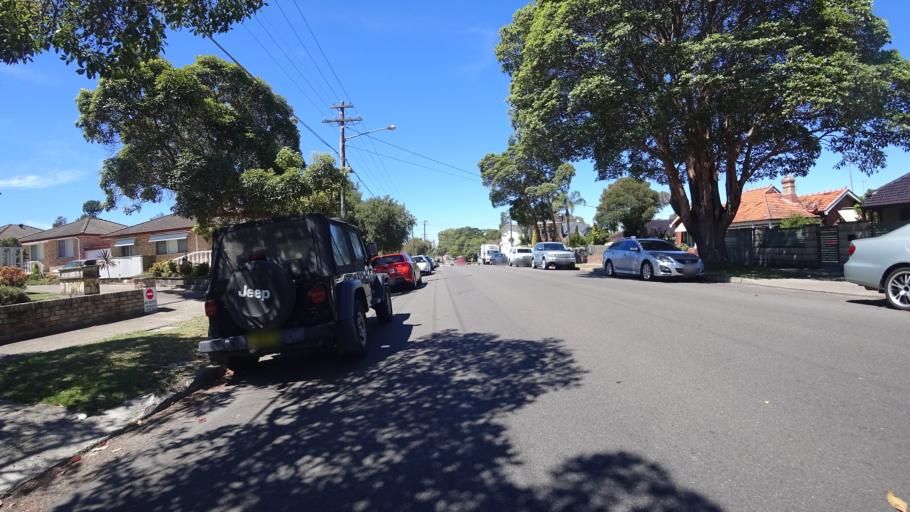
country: AU
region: New South Wales
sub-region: Rockdale
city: Bexley
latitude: -33.9548
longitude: 151.1270
